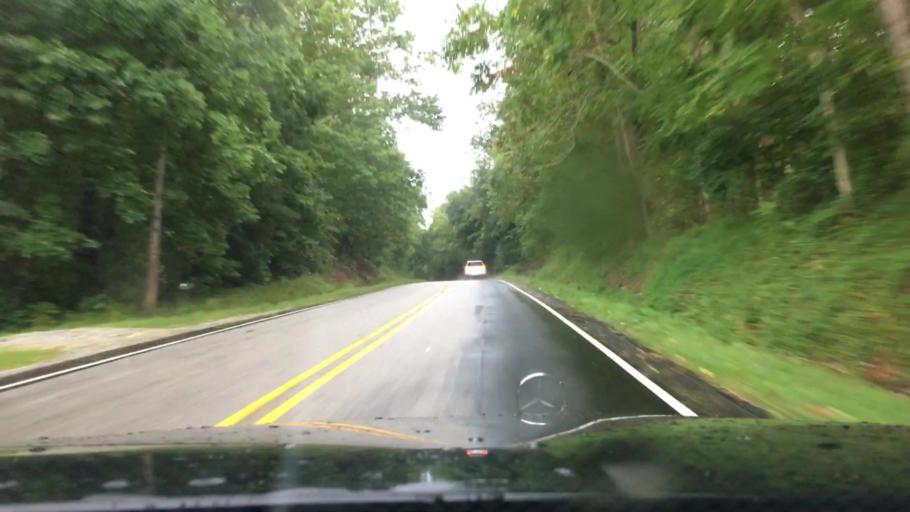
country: US
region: Virginia
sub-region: Amherst County
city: Amherst
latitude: 37.6876
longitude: -79.0253
